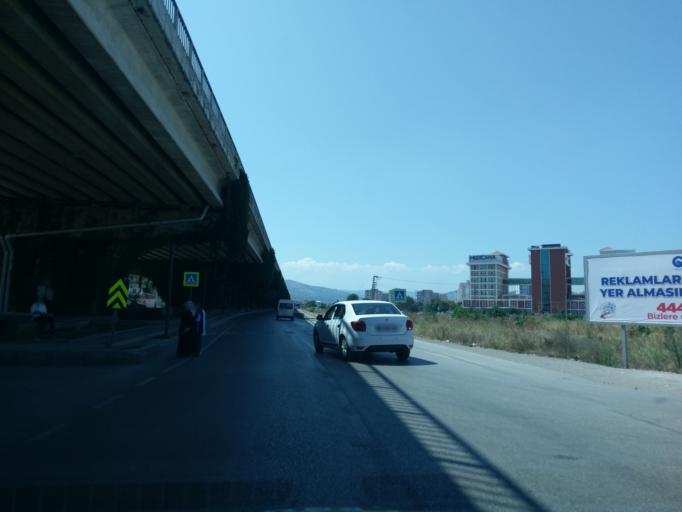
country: TR
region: Samsun
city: Samsun
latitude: 41.2680
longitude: 36.3559
